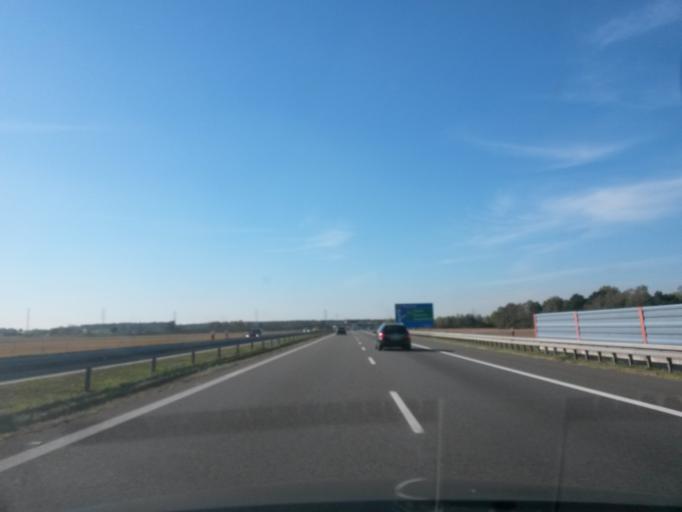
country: PL
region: Opole Voivodeship
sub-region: Powiat krapkowicki
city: Krapkowice
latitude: 50.5259
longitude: 17.9280
